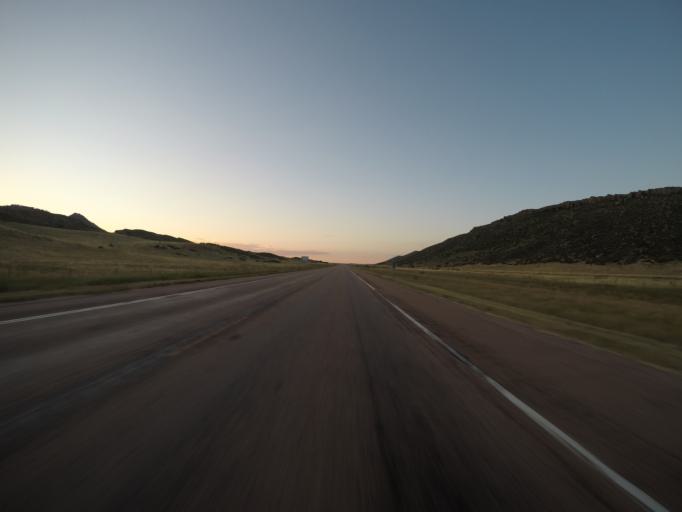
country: US
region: Colorado
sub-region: Larimer County
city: Laporte
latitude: 40.7154
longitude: -105.1724
